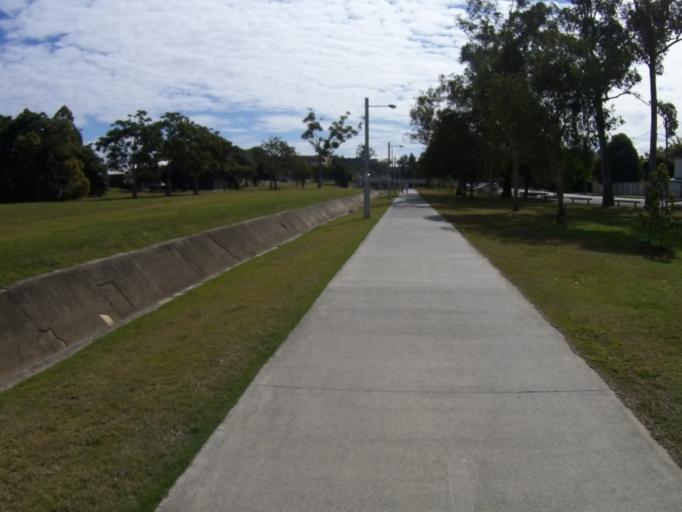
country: AU
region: Queensland
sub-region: Brisbane
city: Greenslopes
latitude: -27.5005
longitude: 153.0424
